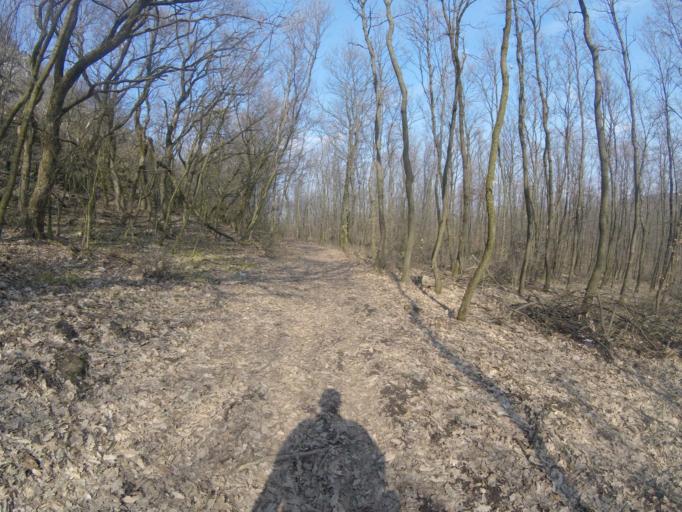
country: HU
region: Komarom-Esztergom
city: Nyergesujfalu
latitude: 47.7279
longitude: 18.5754
